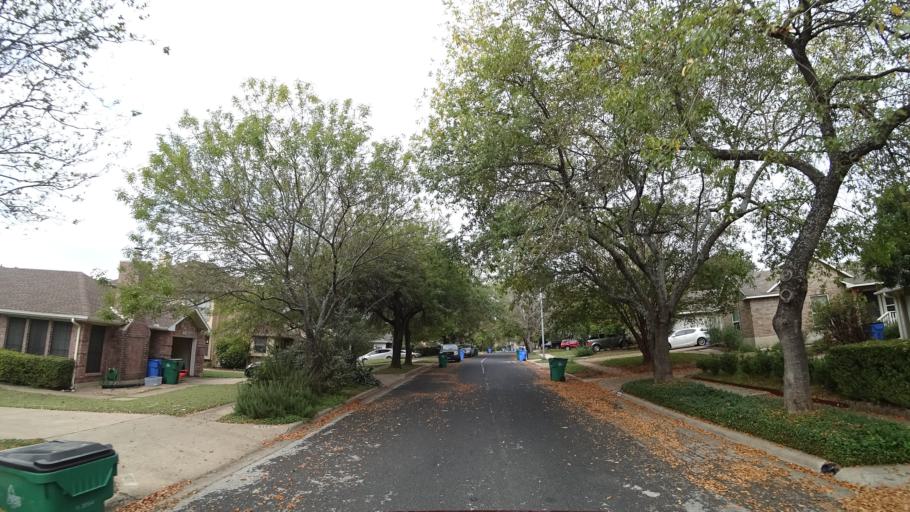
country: US
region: Texas
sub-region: Travis County
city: Wells Branch
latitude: 30.4375
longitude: -97.6838
